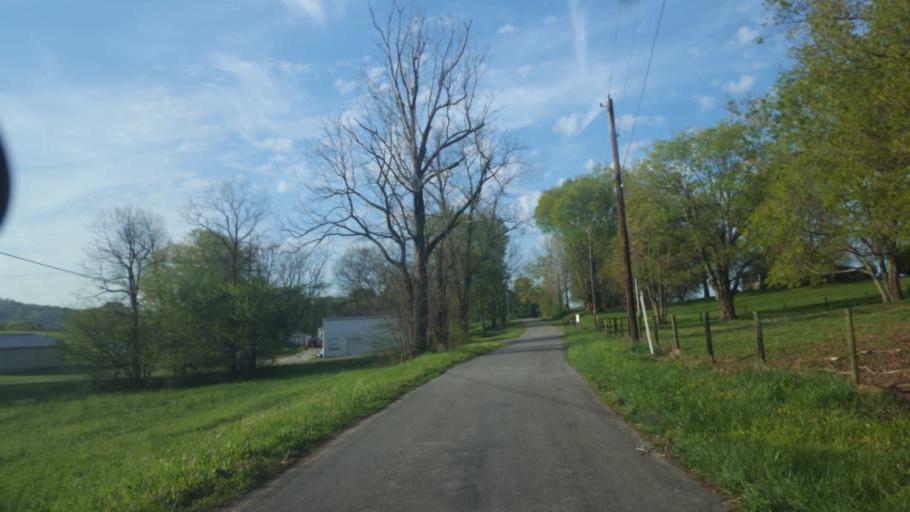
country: US
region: Kentucky
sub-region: Hart County
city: Munfordville
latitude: 37.2613
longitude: -85.8869
